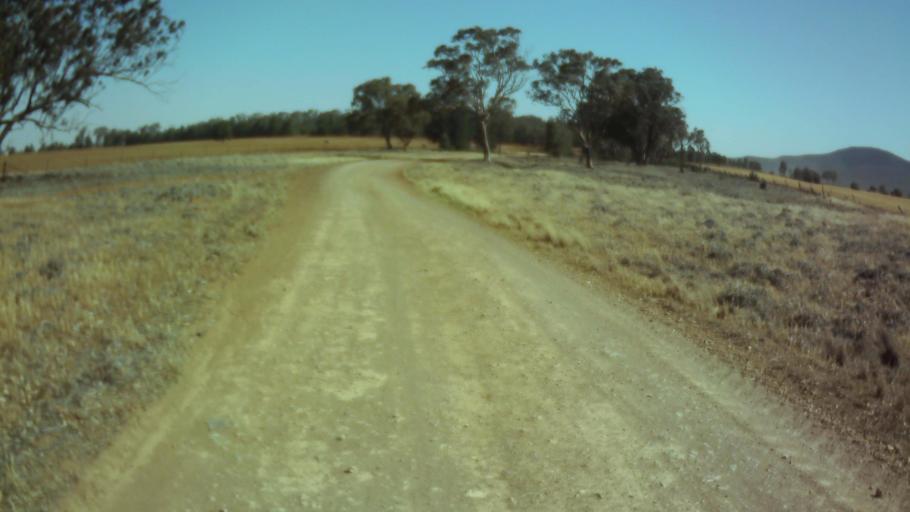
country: AU
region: New South Wales
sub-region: Weddin
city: Grenfell
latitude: -33.8563
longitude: 148.0156
